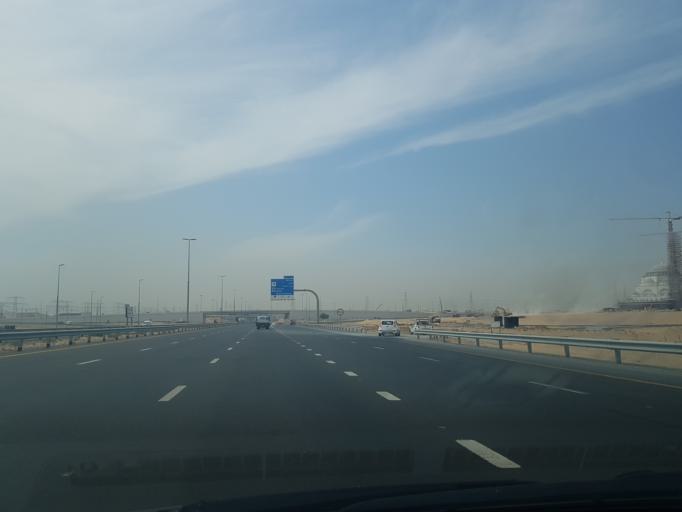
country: AE
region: Ash Shariqah
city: Sharjah
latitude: 25.2359
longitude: 55.5733
